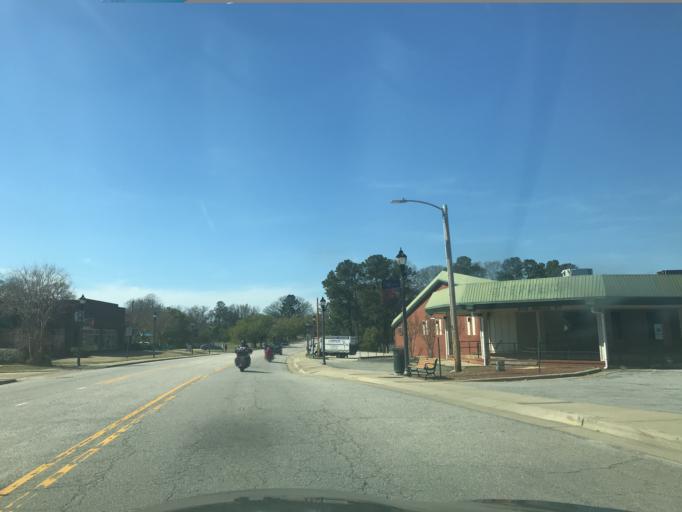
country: US
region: North Carolina
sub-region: Wake County
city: Fuquay-Varina
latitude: 35.5937
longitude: -78.7949
